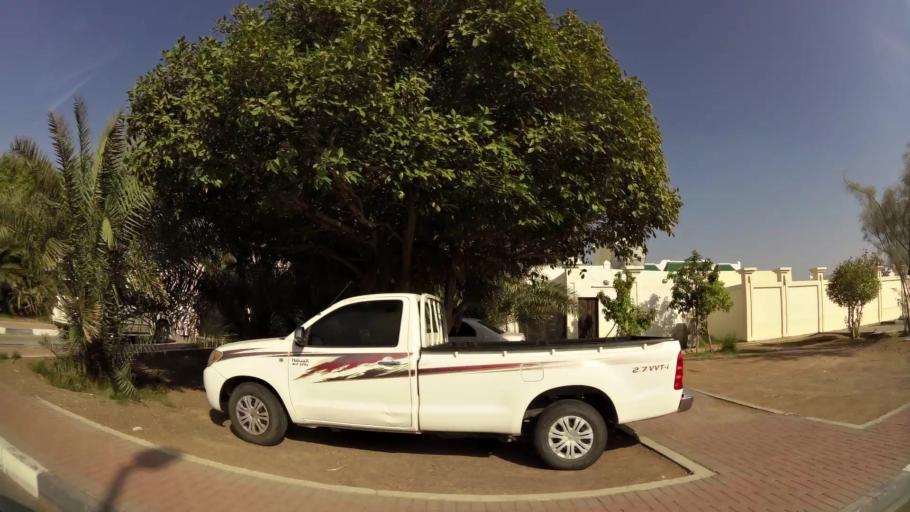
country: AE
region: Abu Dhabi
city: Al Ain
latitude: 24.0841
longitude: 55.8684
